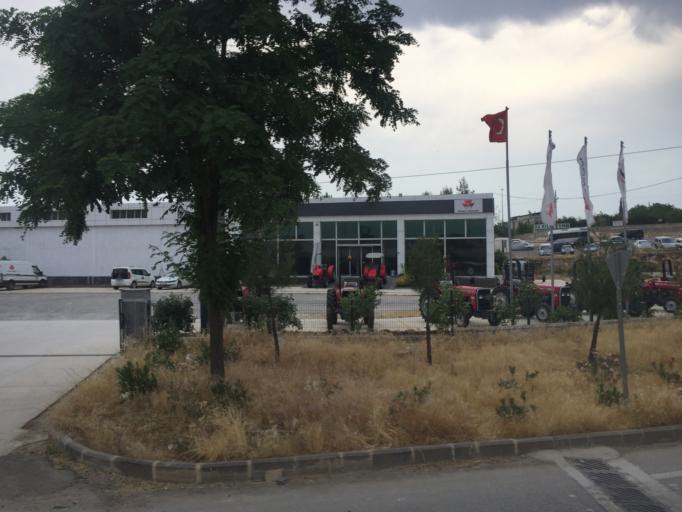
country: TR
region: Gaziantep
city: Gaziantep
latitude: 37.0214
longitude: 37.4286
